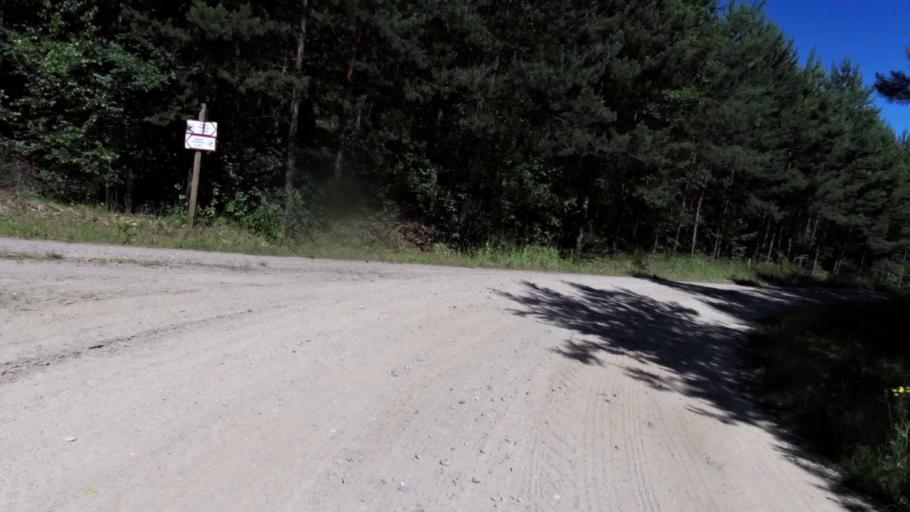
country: PL
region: West Pomeranian Voivodeship
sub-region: Powiat swidwinski
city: Rabino
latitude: 53.8677
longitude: 16.0307
